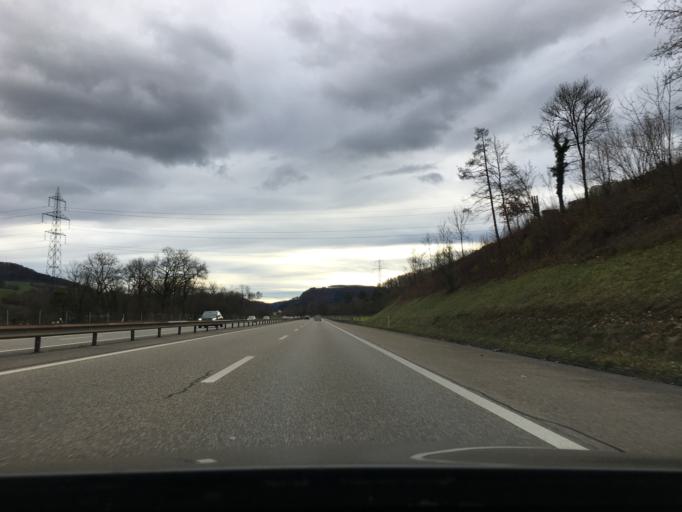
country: CH
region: Aargau
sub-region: Bezirk Laufenburg
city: Eiken
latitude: 47.5280
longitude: 7.9995
